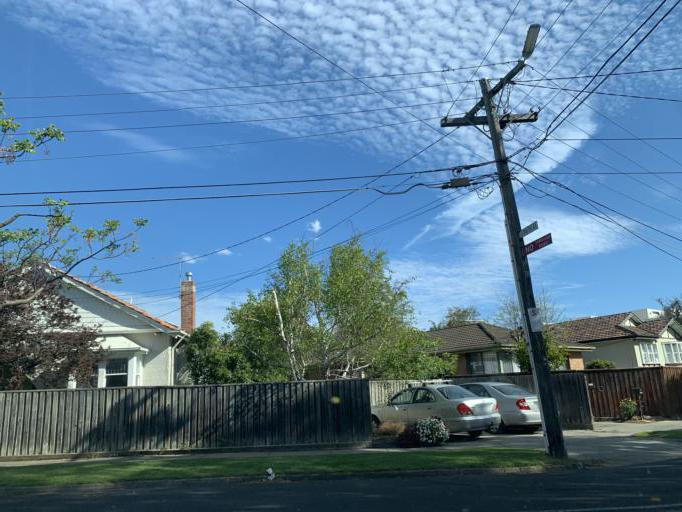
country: AU
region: Victoria
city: Hampton
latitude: -37.9570
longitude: 145.0101
